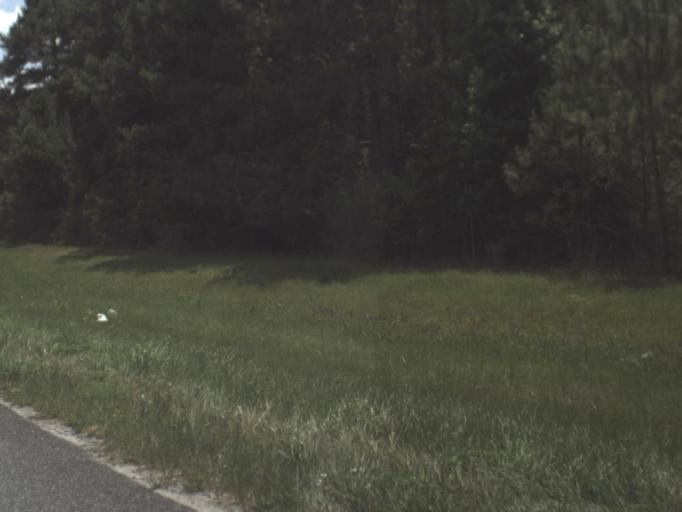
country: US
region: Florida
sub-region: Bradford County
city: Starke
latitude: 30.0148
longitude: -82.0499
